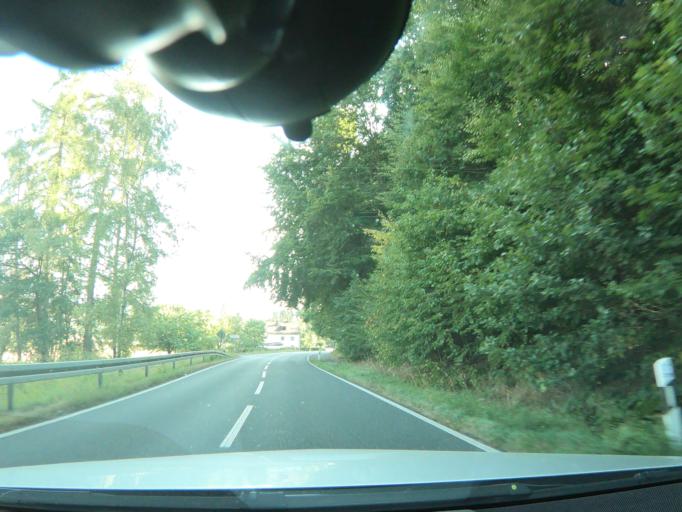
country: DE
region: Hesse
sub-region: Regierungsbezirk Giessen
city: Marburg an der Lahn
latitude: 50.7934
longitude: 8.8170
